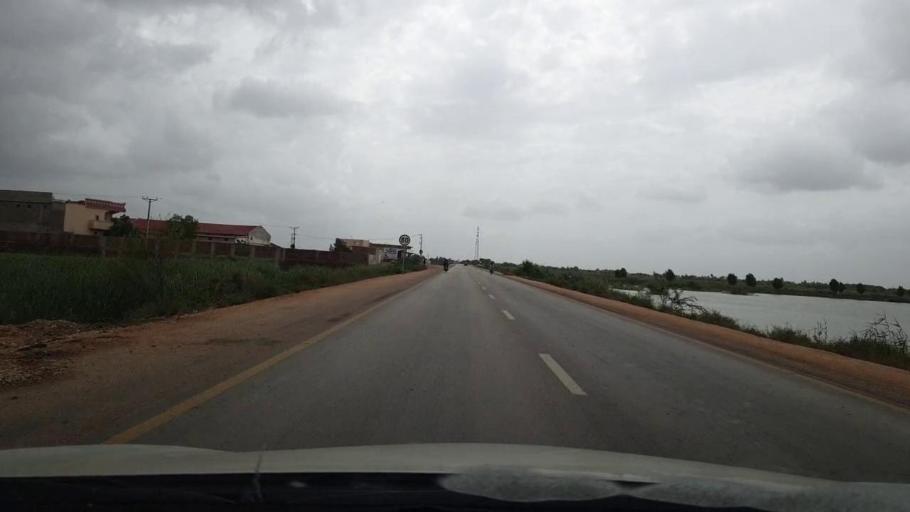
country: PK
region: Sindh
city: Mirpur Batoro
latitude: 24.6192
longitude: 68.3009
